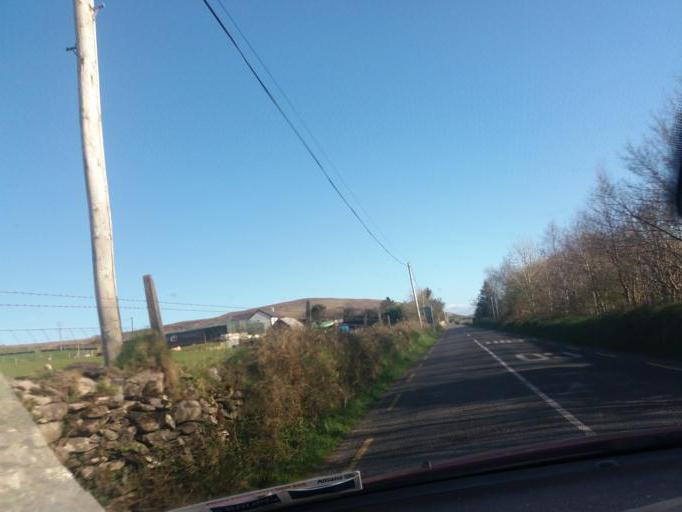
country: IE
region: Munster
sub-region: Ciarrai
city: Dingle
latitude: 52.1675
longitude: -10.2890
